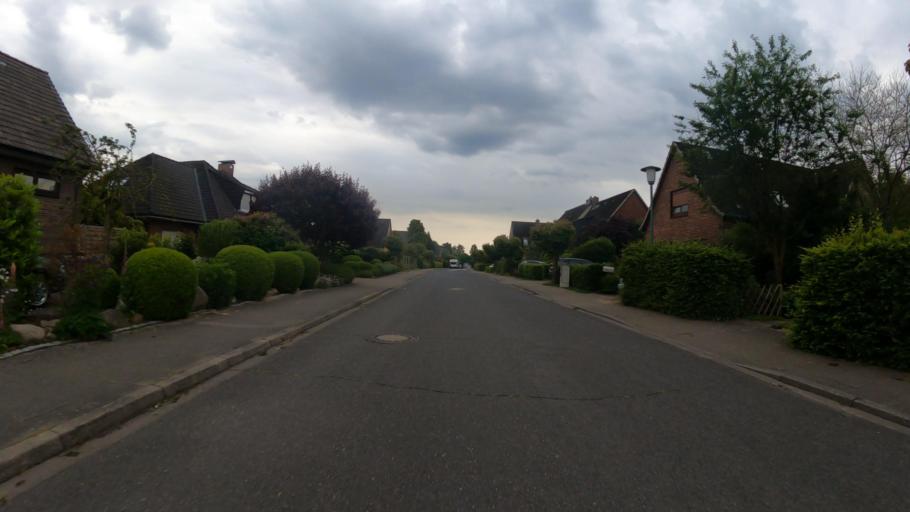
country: DE
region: Schleswig-Holstein
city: Rellingen
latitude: 53.6432
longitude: 9.8192
